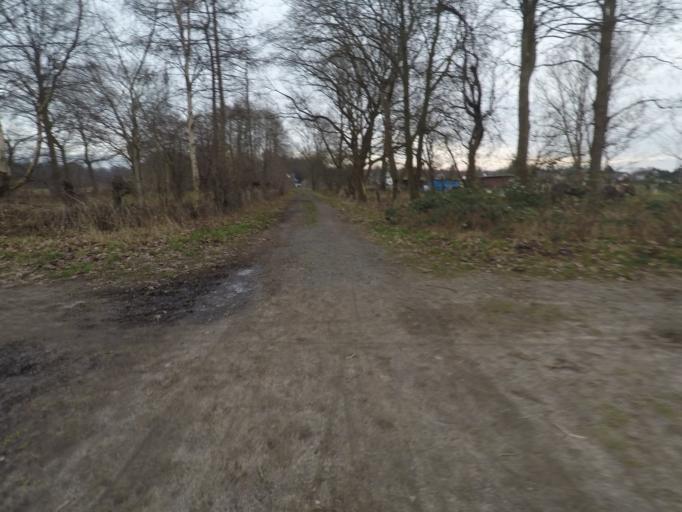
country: DE
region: Lower Saxony
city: Langen
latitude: 53.6022
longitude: 8.6048
